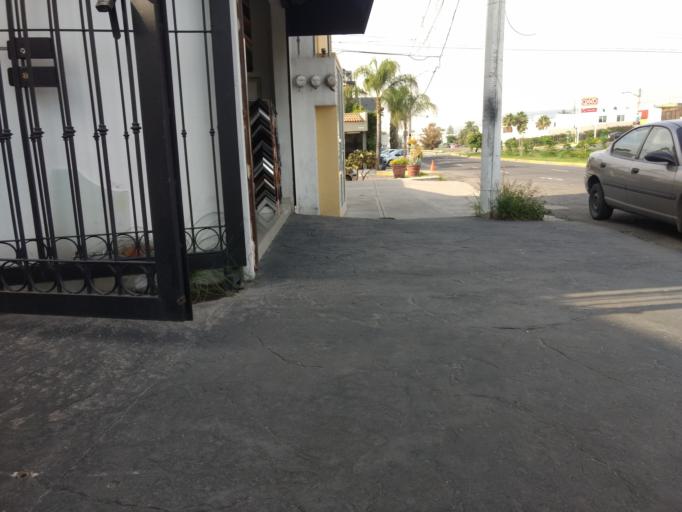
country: MX
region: Jalisco
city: Guadalajara
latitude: 20.6650
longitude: -103.4365
